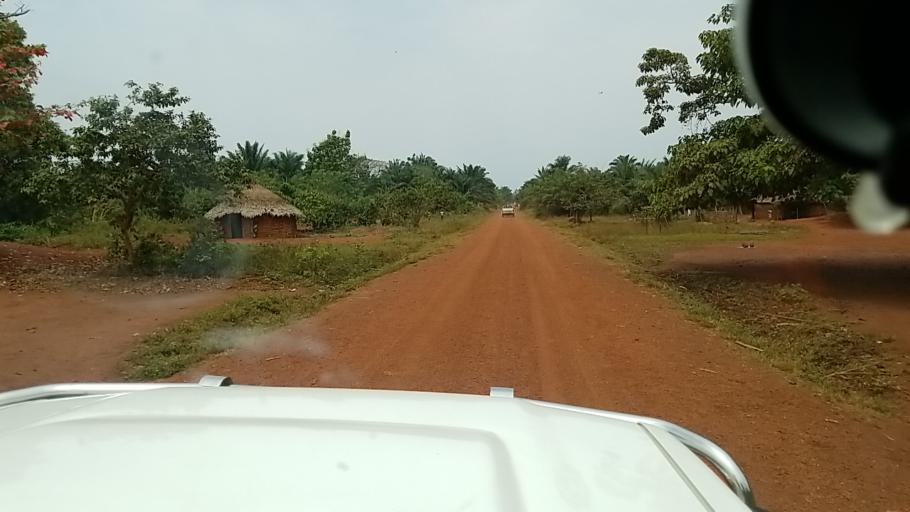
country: CD
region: Equateur
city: Gemena
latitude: 3.5234
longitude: 19.3633
